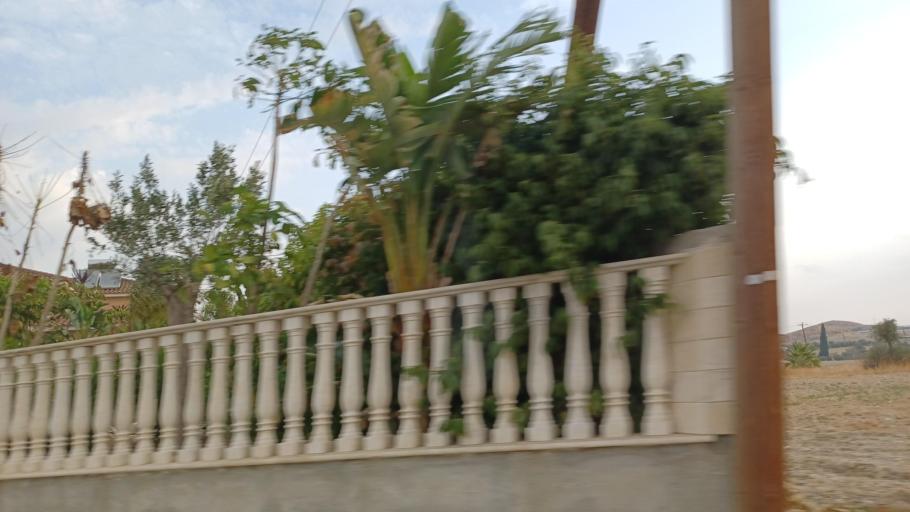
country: CY
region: Larnaka
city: Troulloi
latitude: 35.0111
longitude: 33.5676
